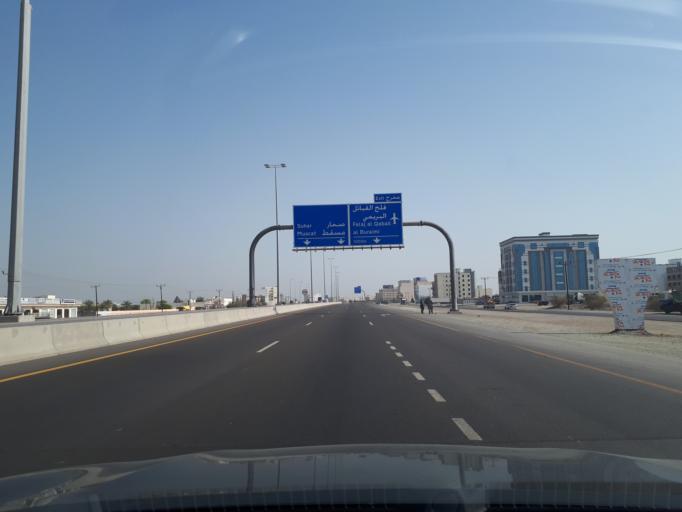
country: OM
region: Al Batinah
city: Al Liwa'
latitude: 24.4392
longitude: 56.6075
